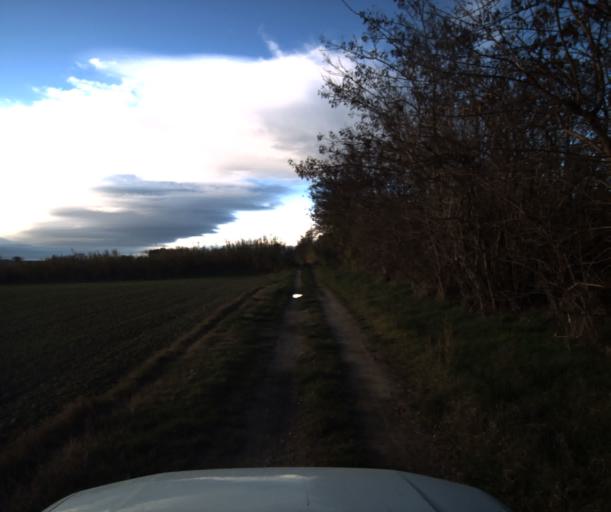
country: FR
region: Provence-Alpes-Cote d'Azur
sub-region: Departement du Vaucluse
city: Pertuis
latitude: 43.6877
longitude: 5.4943
